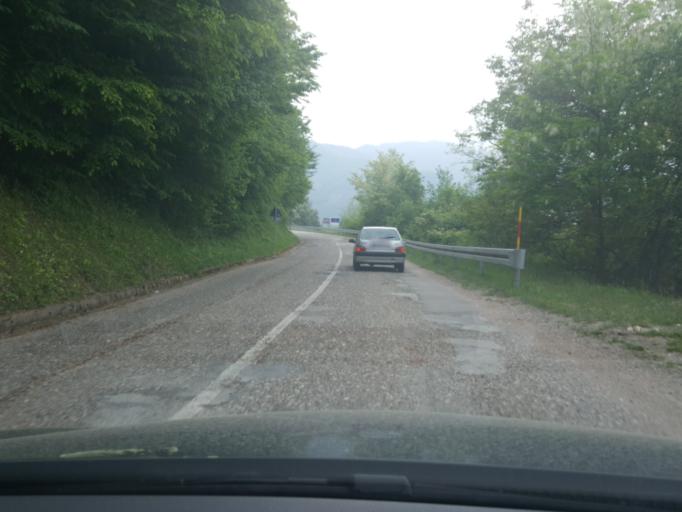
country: RS
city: Kamenica
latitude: 44.2047
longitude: 19.7211
